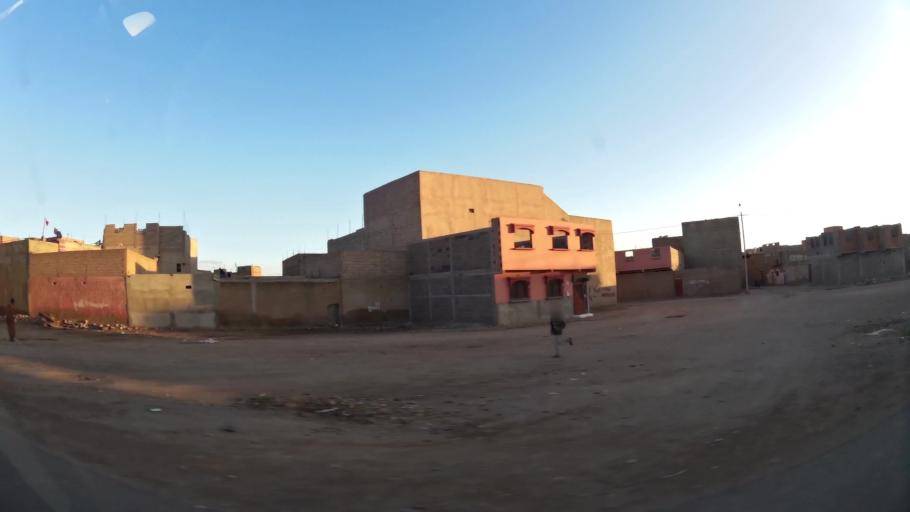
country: MA
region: Marrakech-Tensift-Al Haouz
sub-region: Kelaa-Des-Sraghna
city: Sidi Abdallah
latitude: 32.2393
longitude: -7.9349
